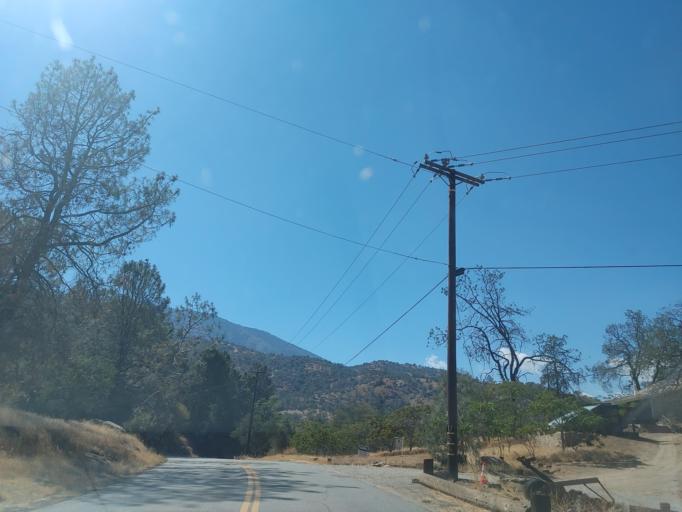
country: US
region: California
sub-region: Kern County
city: Bear Valley Springs
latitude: 35.2233
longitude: -118.5612
